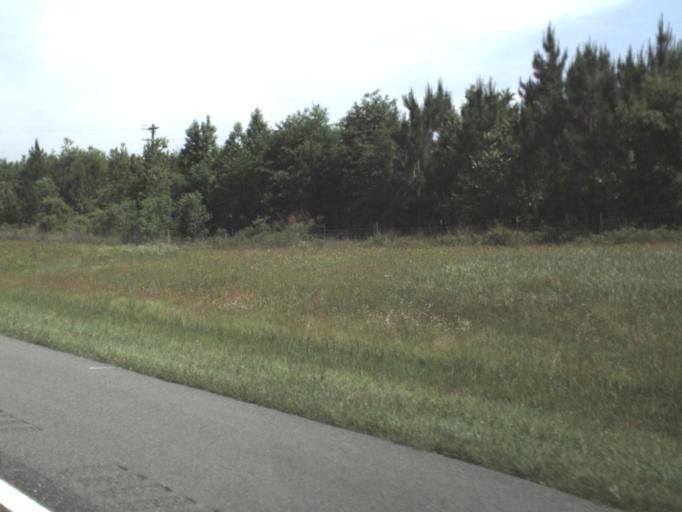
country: US
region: Florida
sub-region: Columbia County
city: Five Points
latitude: 30.2532
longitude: -82.7139
